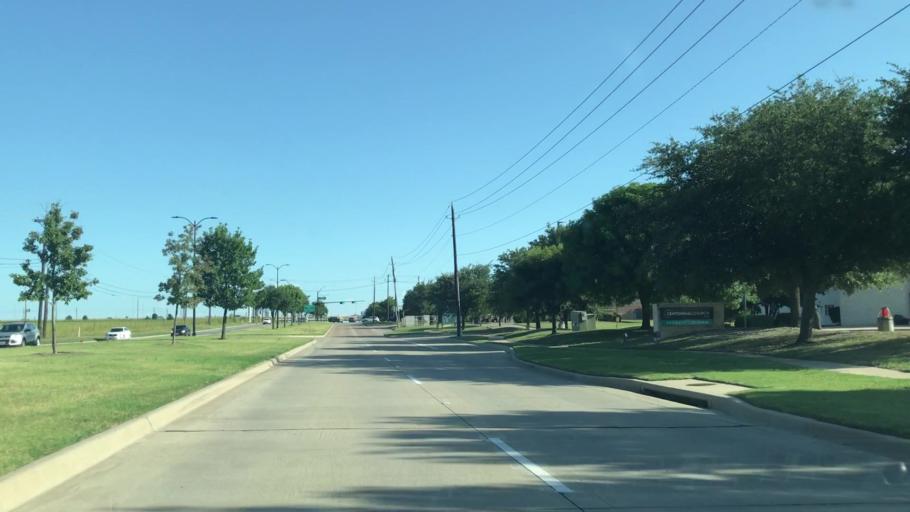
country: US
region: Texas
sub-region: Collin County
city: Frisco
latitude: 33.1181
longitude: -96.7681
